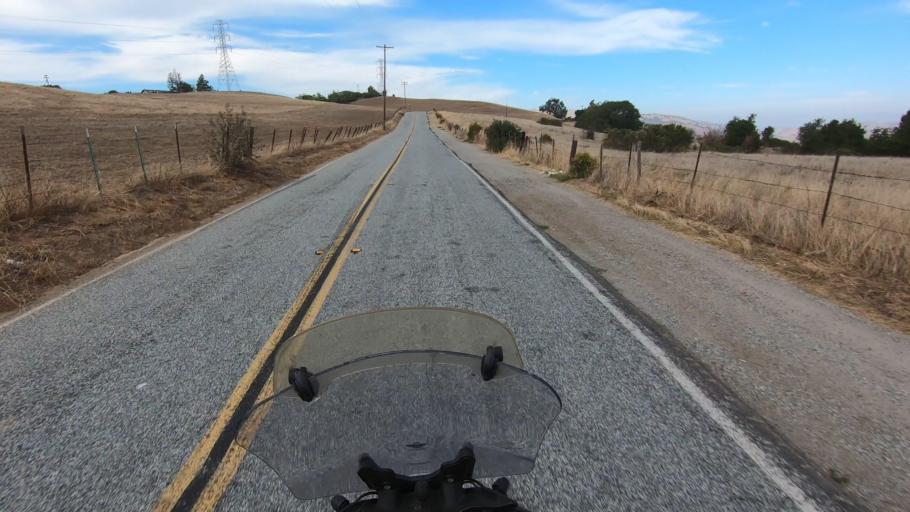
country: US
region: California
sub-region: Santa Clara County
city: East Foothills
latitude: 37.4296
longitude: -121.8012
